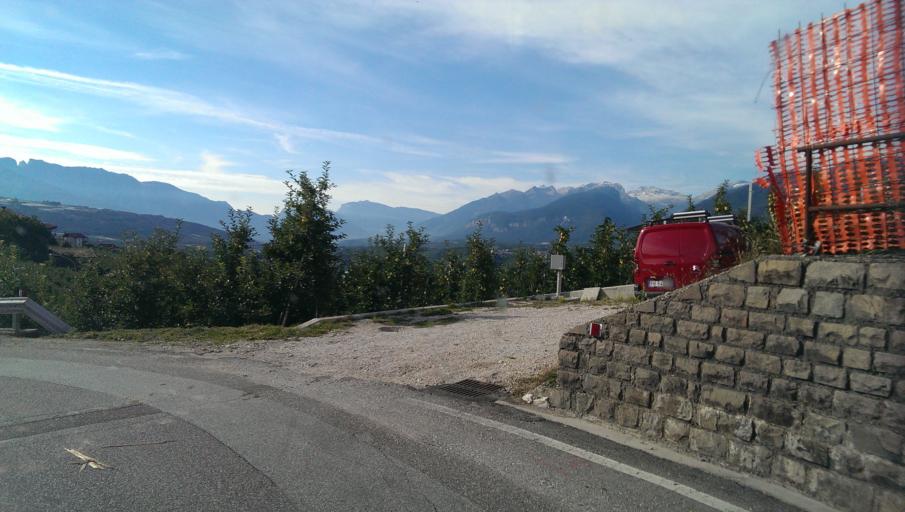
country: IT
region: Trentino-Alto Adige
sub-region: Provincia di Trento
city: Revo
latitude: 46.3937
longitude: 11.0542
